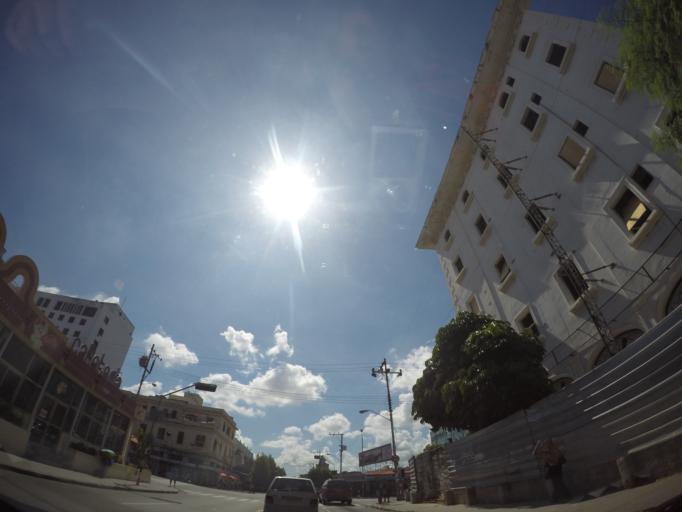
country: CU
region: La Habana
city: Guanabacoa
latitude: 23.0949
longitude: -82.3160
